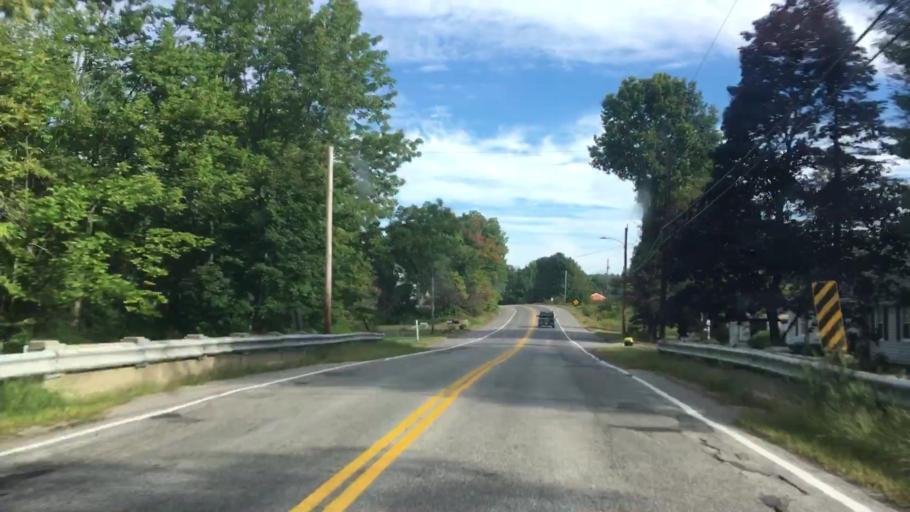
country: US
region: Maine
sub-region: Cumberland County
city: Cumberland Center
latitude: 43.7517
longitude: -70.2991
